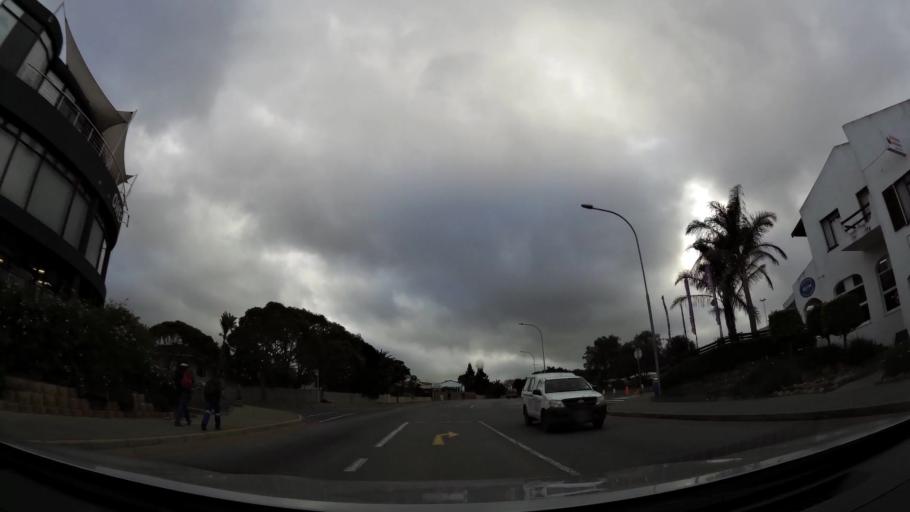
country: ZA
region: Western Cape
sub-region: Eden District Municipality
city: Plettenberg Bay
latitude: -34.0564
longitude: 23.3706
